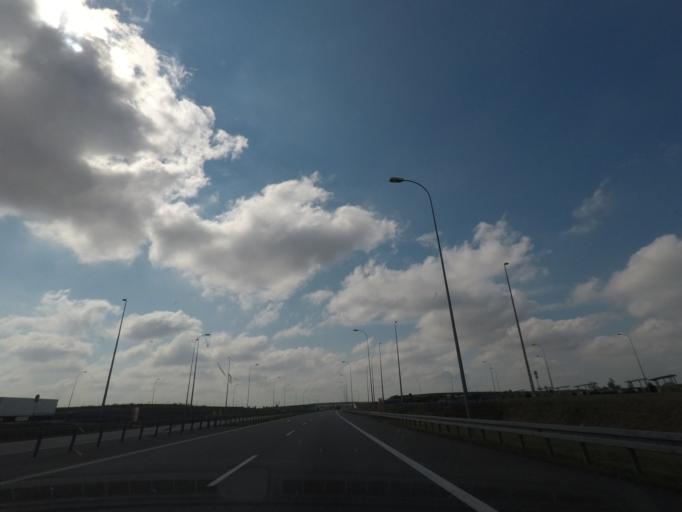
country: PL
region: Kujawsko-Pomorskie
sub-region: Powiat chelminski
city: Lisewo
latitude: 53.2591
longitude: 18.7243
